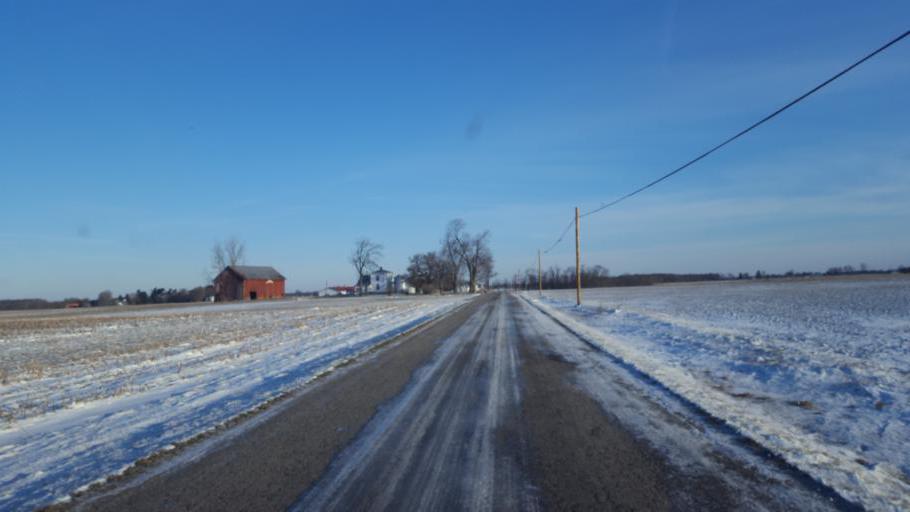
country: US
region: Ohio
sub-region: Morrow County
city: Cardington
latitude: 40.5220
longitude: -82.9033
